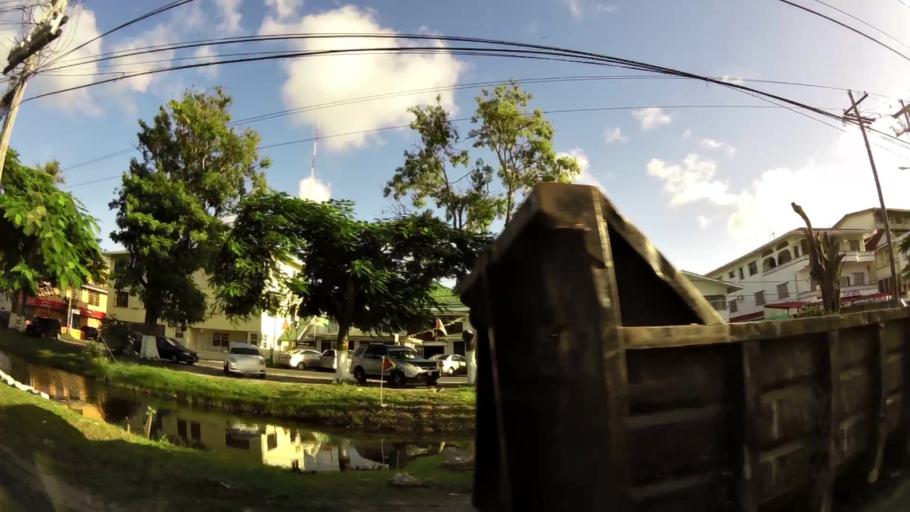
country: GY
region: Demerara-Mahaica
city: Georgetown
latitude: 6.8084
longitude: -58.1604
